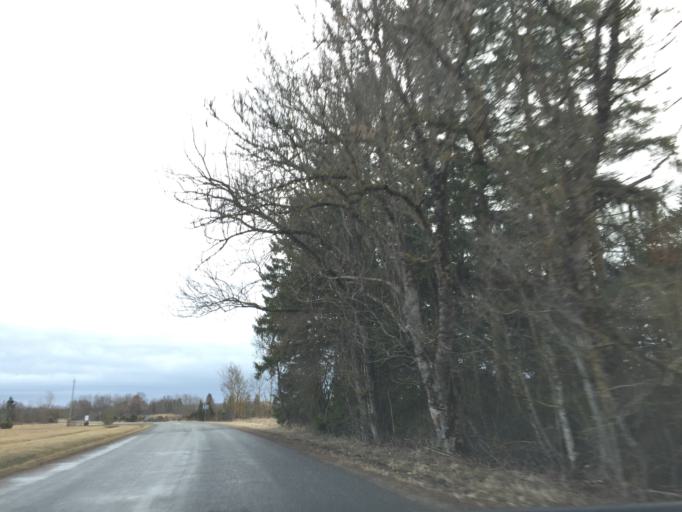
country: EE
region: Laeaene
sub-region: Haapsalu linn
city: Haapsalu
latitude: 58.8166
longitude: 23.5517
